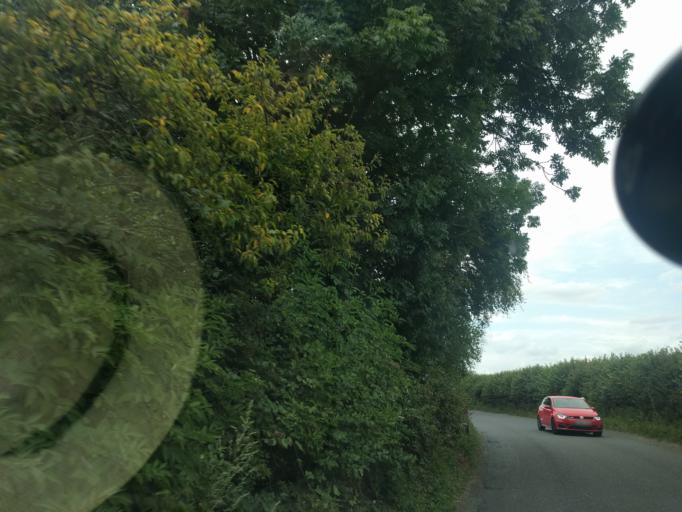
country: GB
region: England
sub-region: Wiltshire
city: Lacock
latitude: 51.4048
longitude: -2.1022
